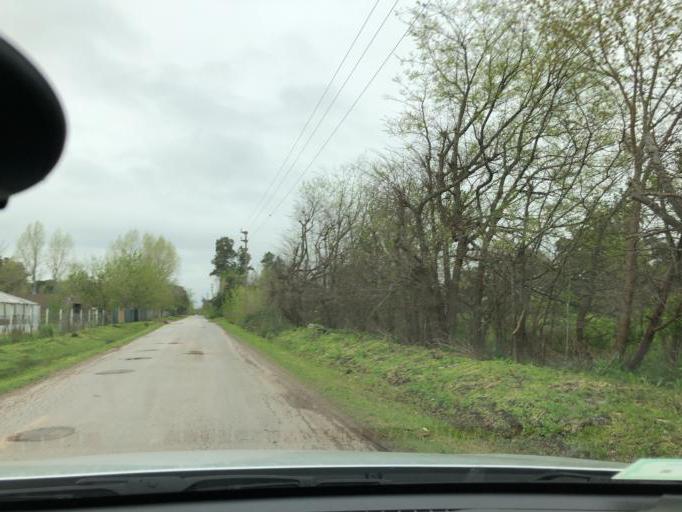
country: AR
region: Buenos Aires
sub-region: Partido de La Plata
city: La Plata
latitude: -34.9000
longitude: -58.0911
